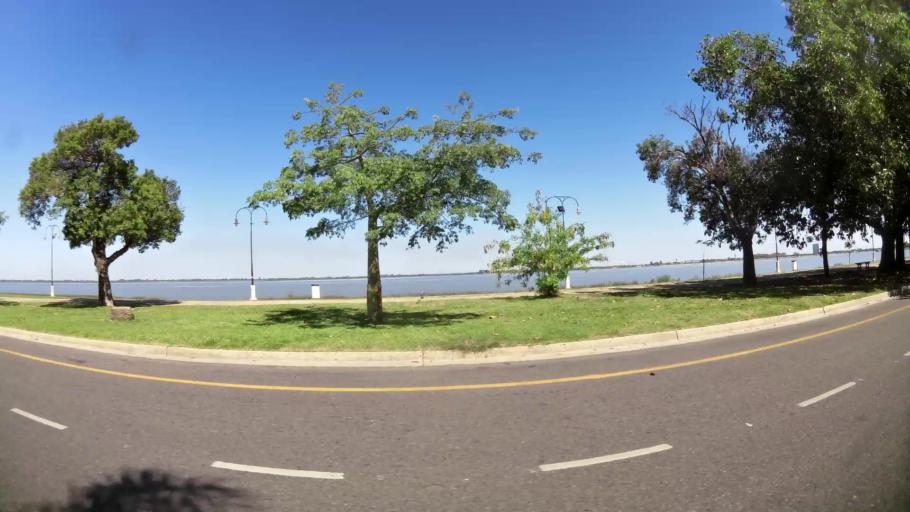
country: AR
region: Santa Fe
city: Santa Fe de la Vera Cruz
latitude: -31.6157
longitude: -60.6725
